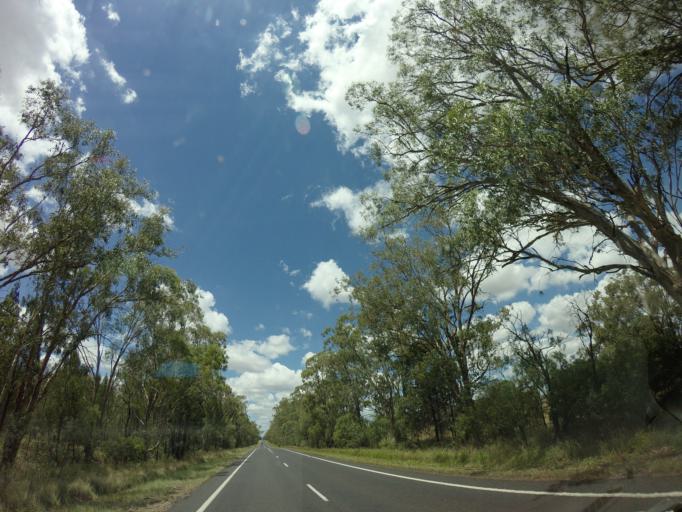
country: AU
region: Queensland
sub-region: Toowoomba
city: Oakey
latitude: -27.8985
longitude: 151.2021
